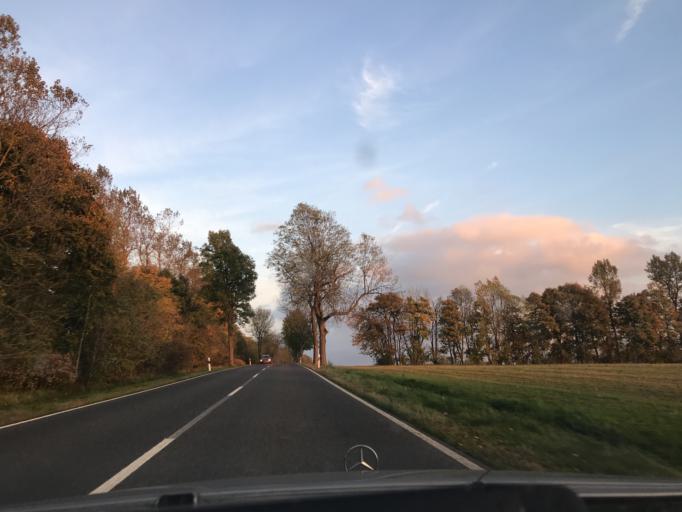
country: DE
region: Thuringia
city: Kreuzebra
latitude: 51.3375
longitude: 10.2693
